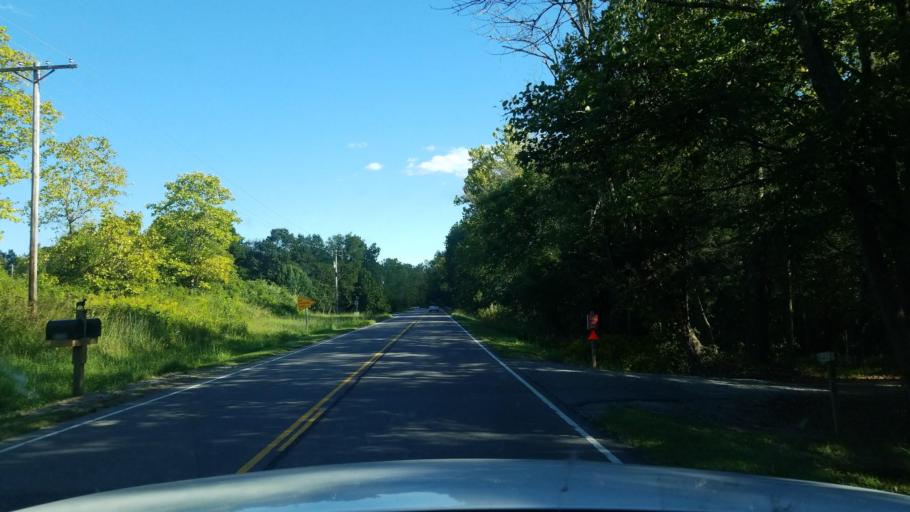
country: US
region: Illinois
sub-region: Saline County
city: Harrisburg
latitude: 37.6047
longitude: -88.4610
